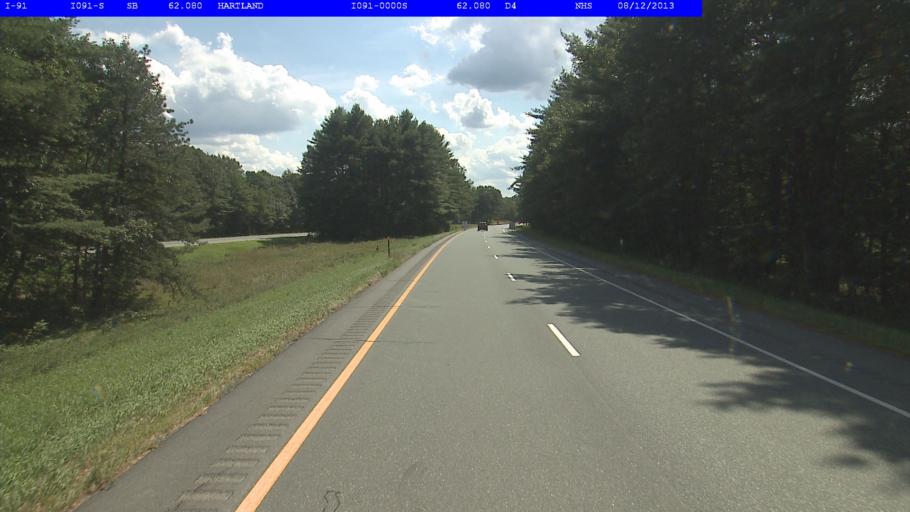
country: US
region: Vermont
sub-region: Windsor County
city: Windsor
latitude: 43.5474
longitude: -72.3857
